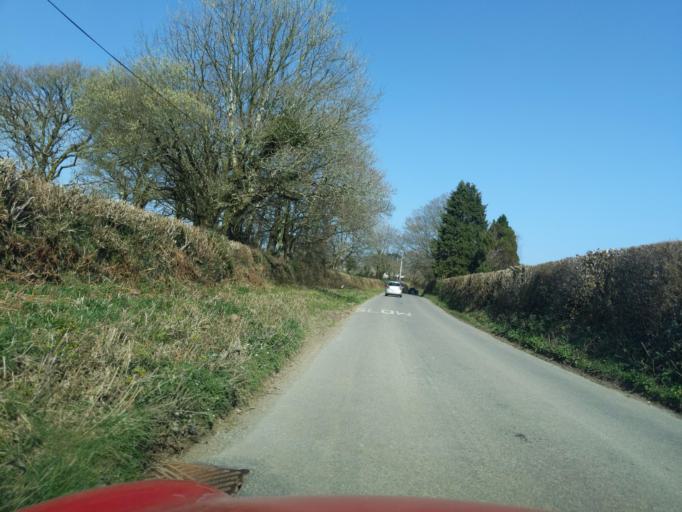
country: GB
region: England
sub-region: Devon
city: Horrabridge
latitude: 50.4874
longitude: -4.1200
